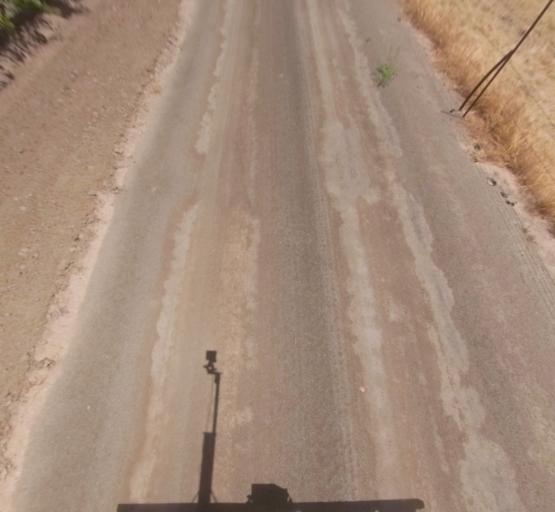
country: US
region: California
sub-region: Madera County
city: Fairmead
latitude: 37.0329
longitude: -120.2370
